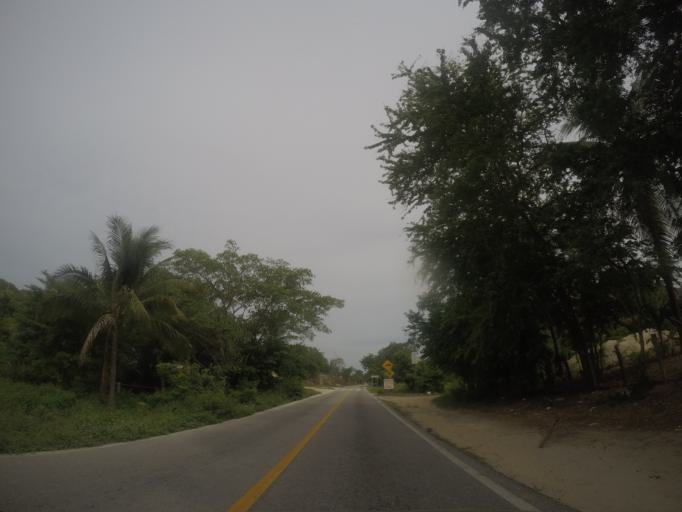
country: MX
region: Oaxaca
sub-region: Villa de Tututepec de Melchor Ocampo
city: Santa Rosa de Lima
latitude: 15.9707
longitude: -97.3982
